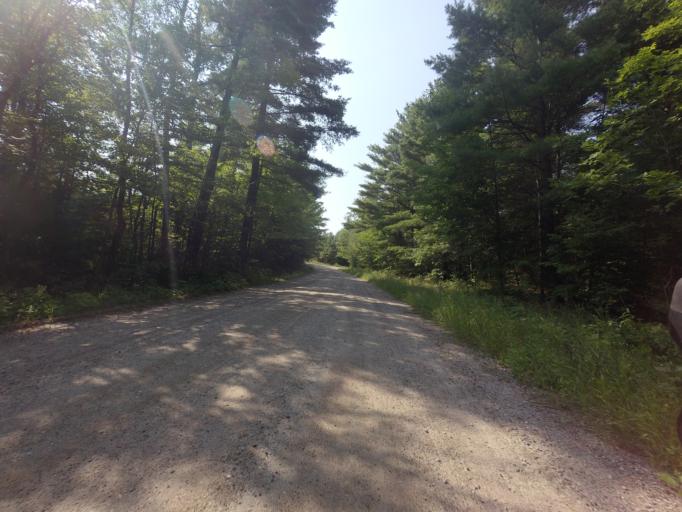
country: CA
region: Ontario
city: Skatepark
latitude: 44.7250
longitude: -76.7826
